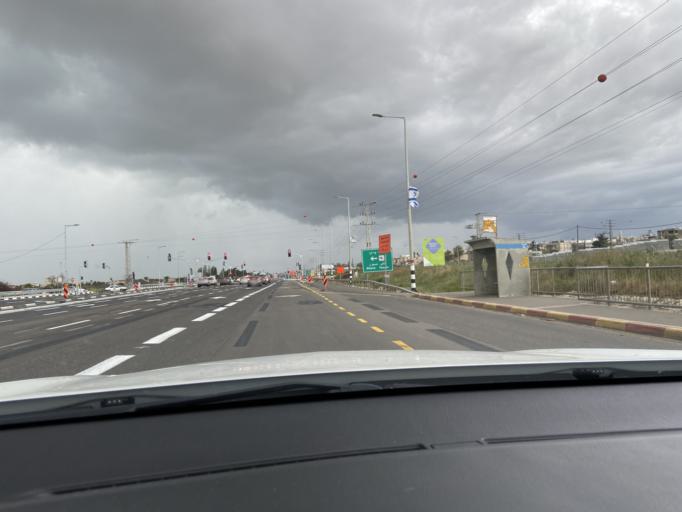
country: IL
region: Northern District
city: El Mazra`a
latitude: 32.9784
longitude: 35.0939
